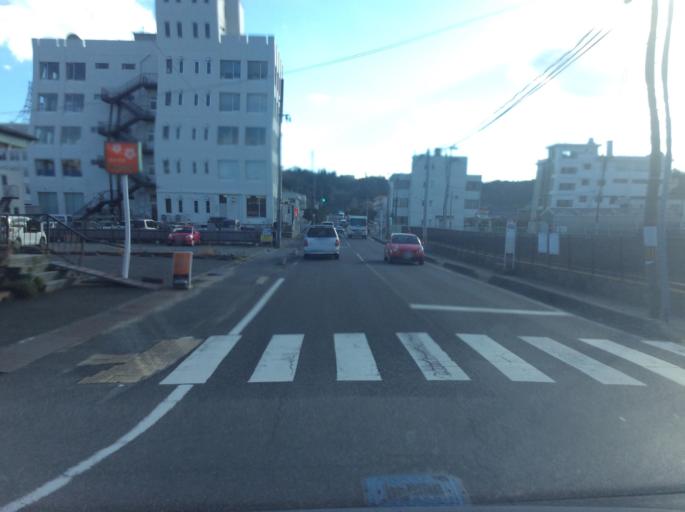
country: JP
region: Fukushima
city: Iwaki
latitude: 37.0520
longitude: 140.8848
